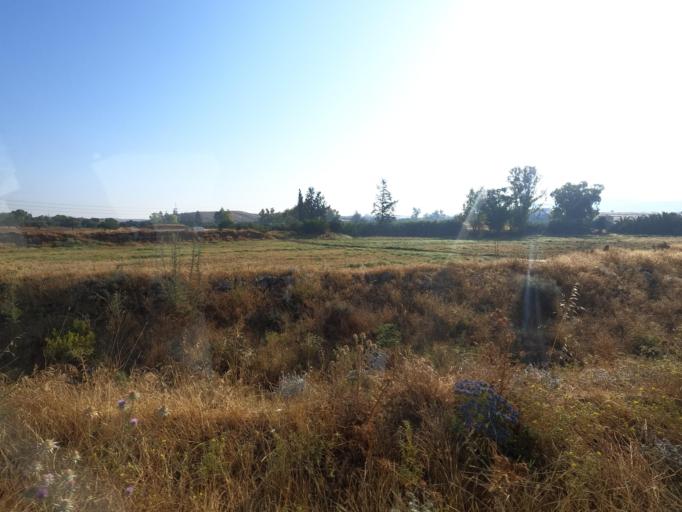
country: CY
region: Larnaka
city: Mosfiloti
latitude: 34.9802
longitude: 33.4373
